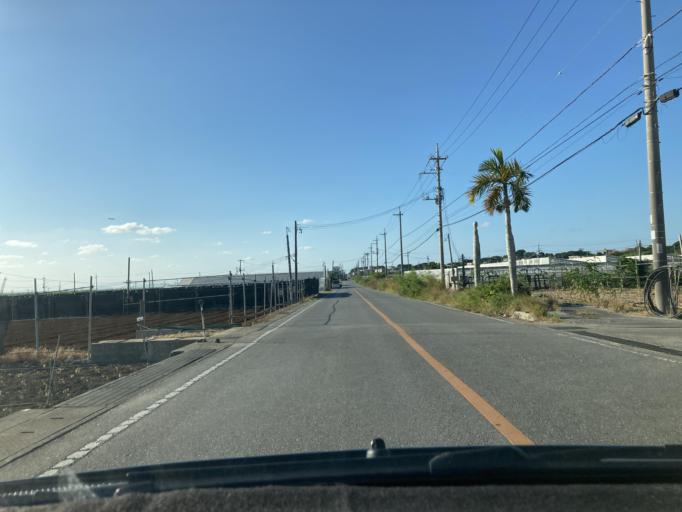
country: JP
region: Okinawa
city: Itoman
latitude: 26.1012
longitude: 127.6726
